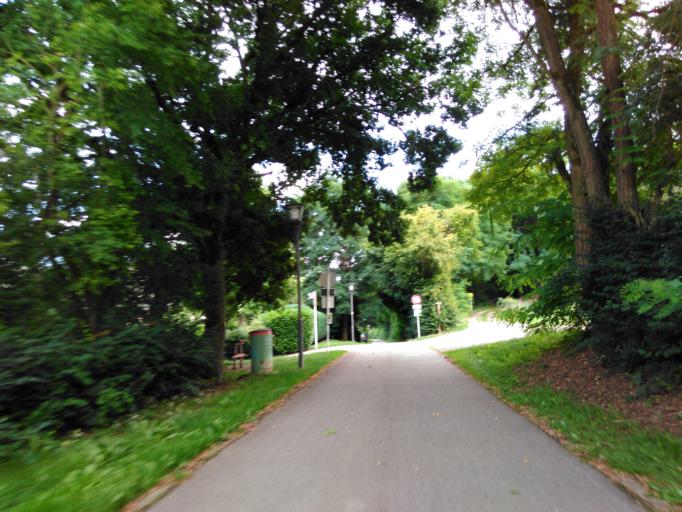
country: DE
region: Rheinland-Pfalz
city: Menningen
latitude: 49.8176
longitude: 6.4750
